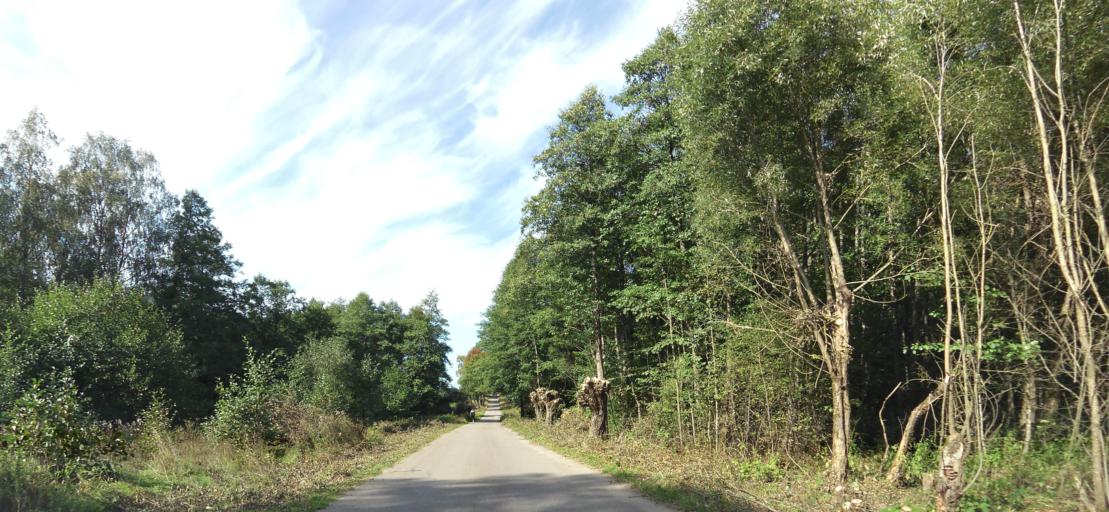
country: LT
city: Salcininkai
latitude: 54.4488
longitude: 25.5170
